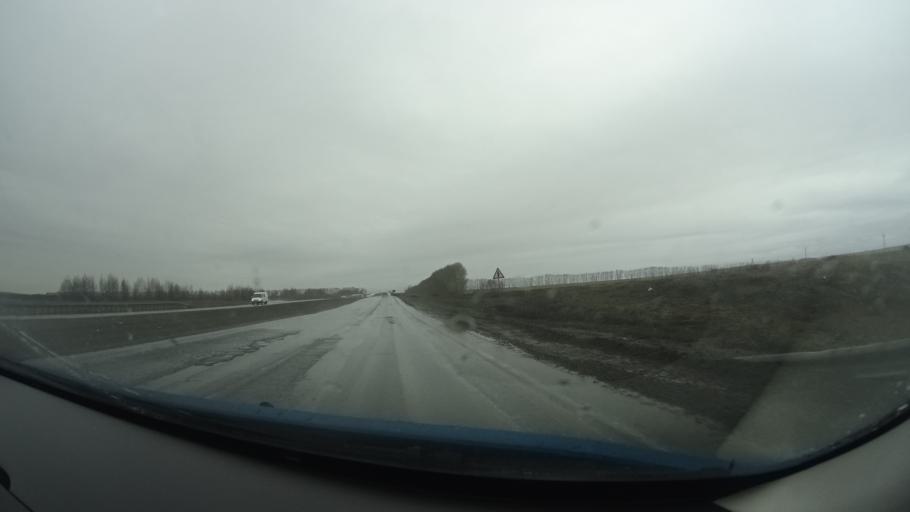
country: RU
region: Bashkortostan
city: Chishmy
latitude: 54.6641
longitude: 55.4297
